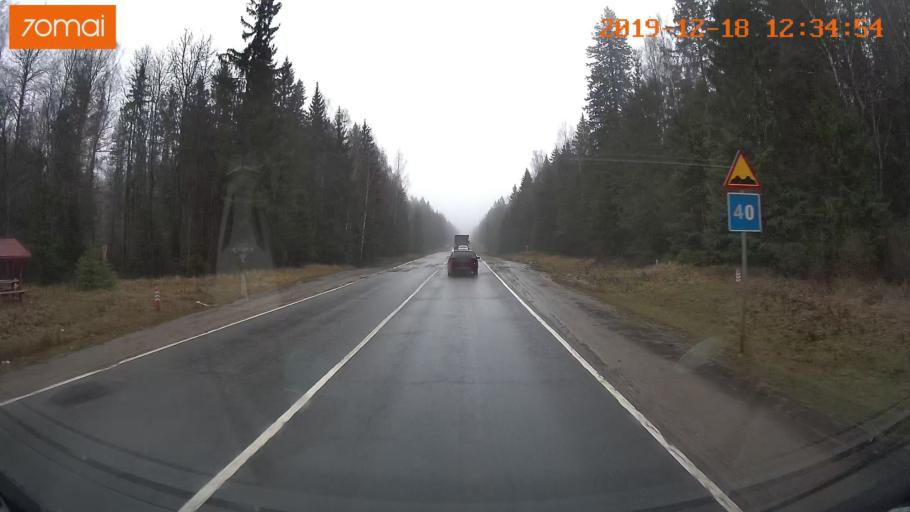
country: RU
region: Moskovskaya
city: Rumyantsevo
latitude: 56.1248
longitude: 36.5771
